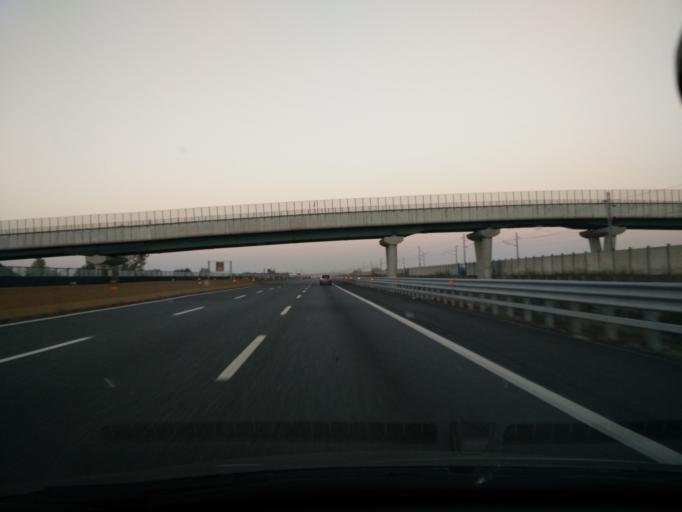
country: IT
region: Piedmont
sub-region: Provincia di Vercelli
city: Saluggia
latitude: 45.2640
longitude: 8.0107
